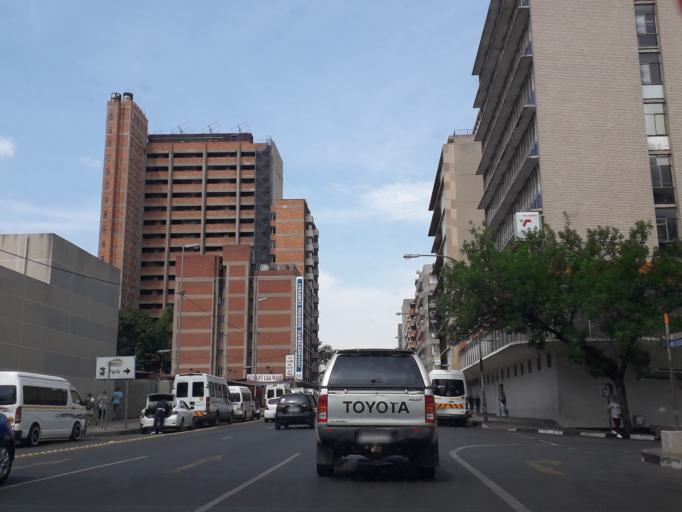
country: ZA
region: Gauteng
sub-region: City of Johannesburg Metropolitan Municipality
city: Johannesburg
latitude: -26.1945
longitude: 28.0422
